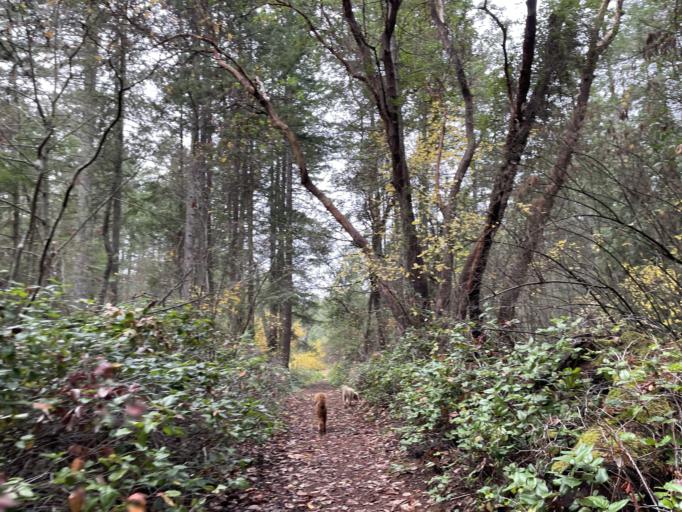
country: CA
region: British Columbia
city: North Cowichan
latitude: 48.9392
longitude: -123.5464
